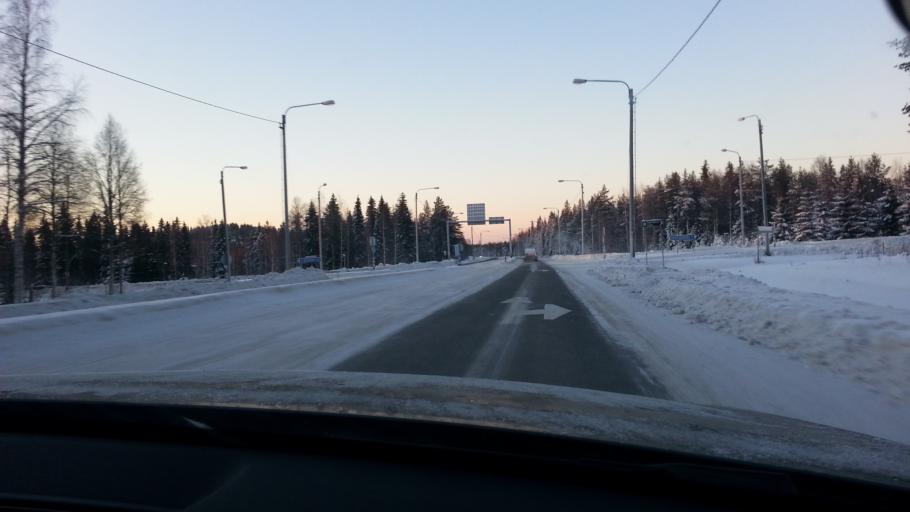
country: FI
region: Lapland
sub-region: Rovaniemi
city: Rovaniemi
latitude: 66.5426
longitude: 25.8196
